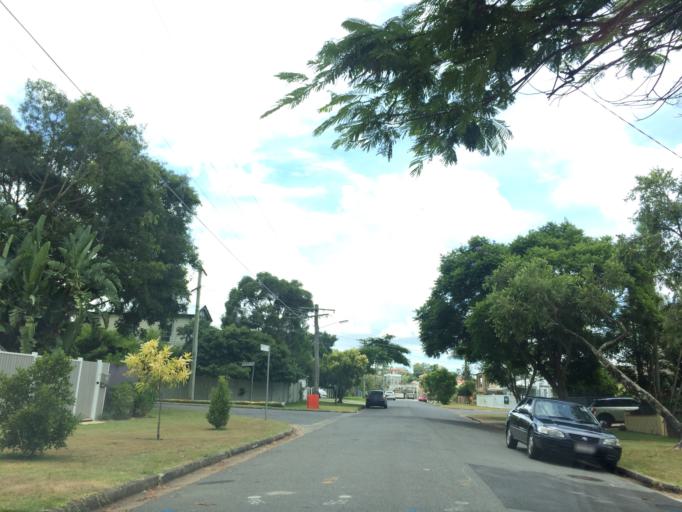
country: AU
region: Queensland
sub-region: Brisbane
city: Ascot
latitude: -27.4449
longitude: 153.0599
